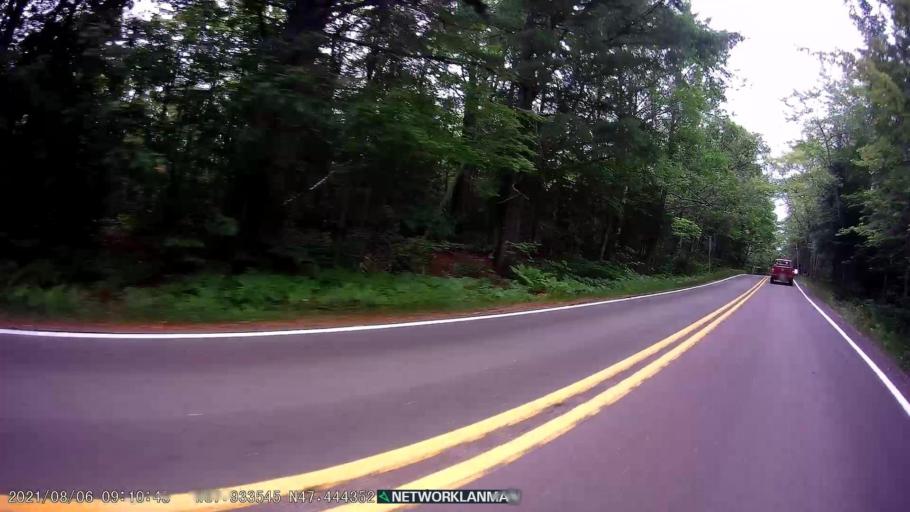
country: US
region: Michigan
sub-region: Keweenaw County
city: Eagle River
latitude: 47.4444
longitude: -87.9329
